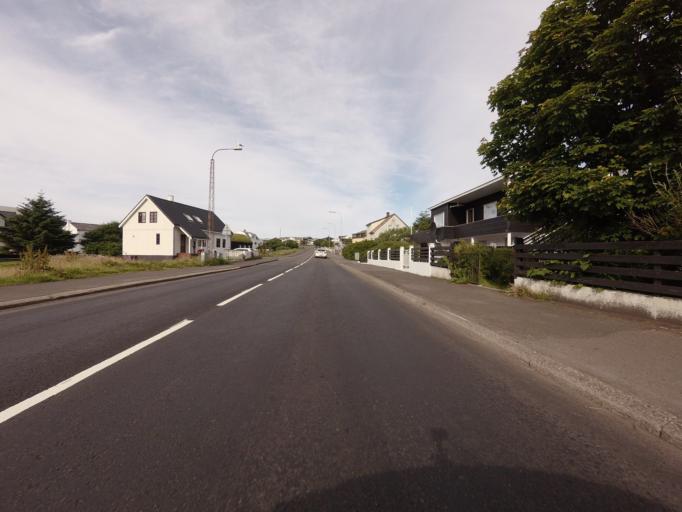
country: FO
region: Vagar
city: Midvagur
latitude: 62.0483
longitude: -7.1967
